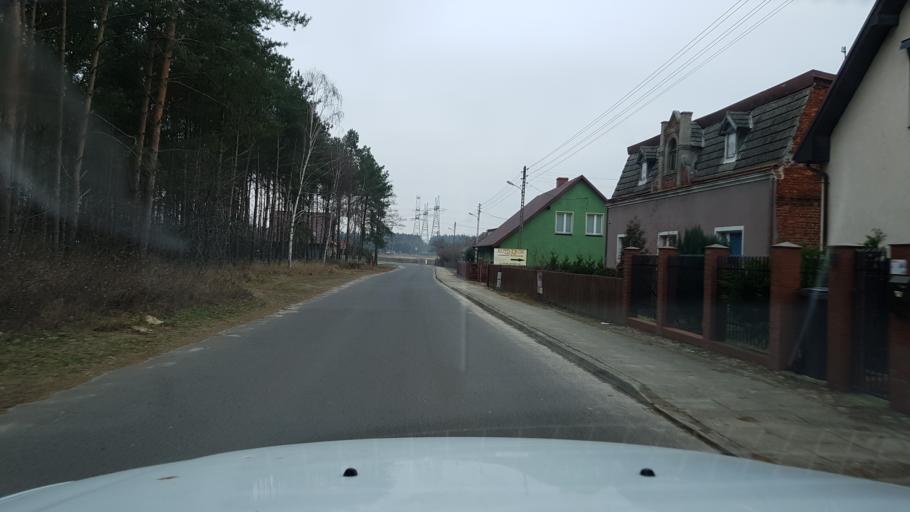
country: PL
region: West Pomeranian Voivodeship
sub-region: Powiat gryfinski
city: Gryfino
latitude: 53.1951
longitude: 14.4839
